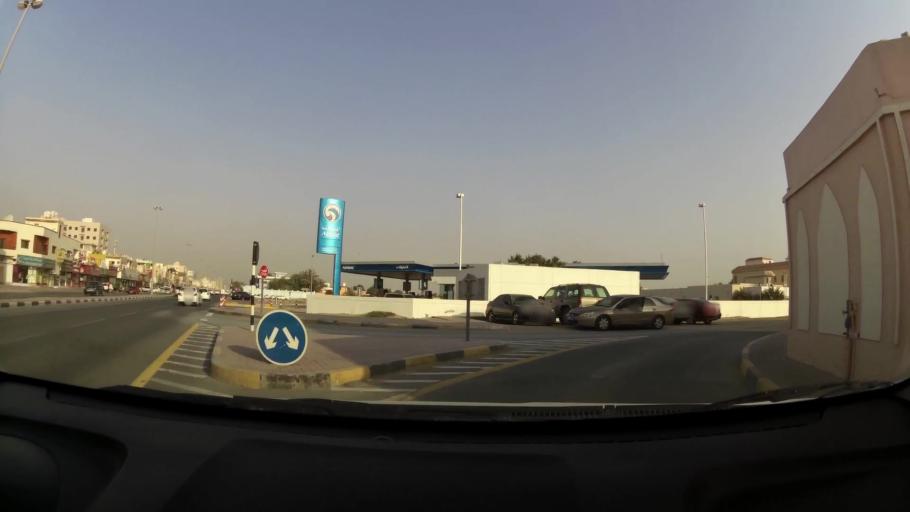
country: AE
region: Ajman
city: Ajman
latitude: 25.3852
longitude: 55.4415
